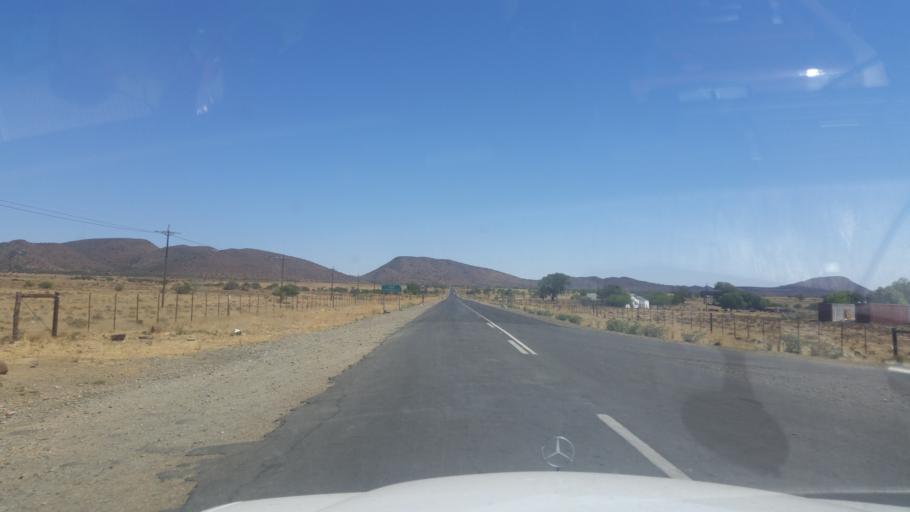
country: ZA
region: Northern Cape
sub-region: Pixley ka Seme District Municipality
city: Colesberg
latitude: -30.6332
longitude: 25.4514
